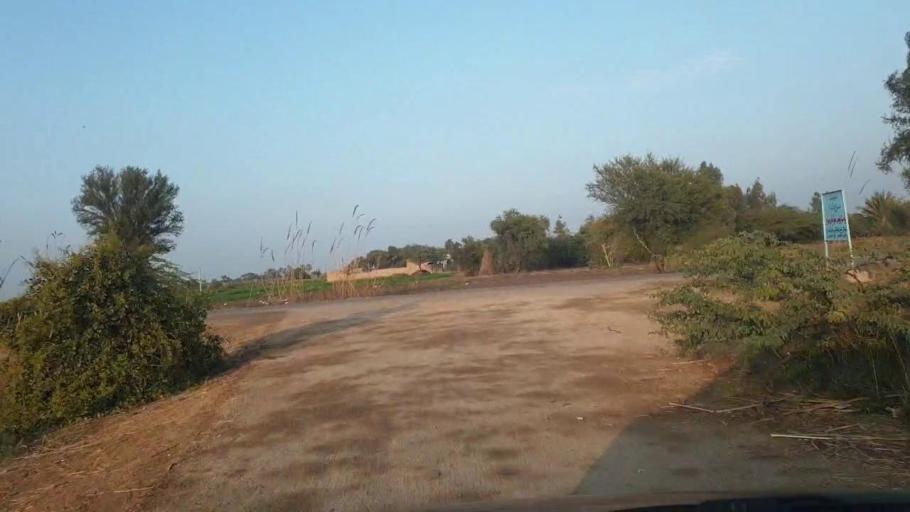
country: PK
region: Sindh
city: Berani
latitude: 25.8407
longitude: 68.7304
